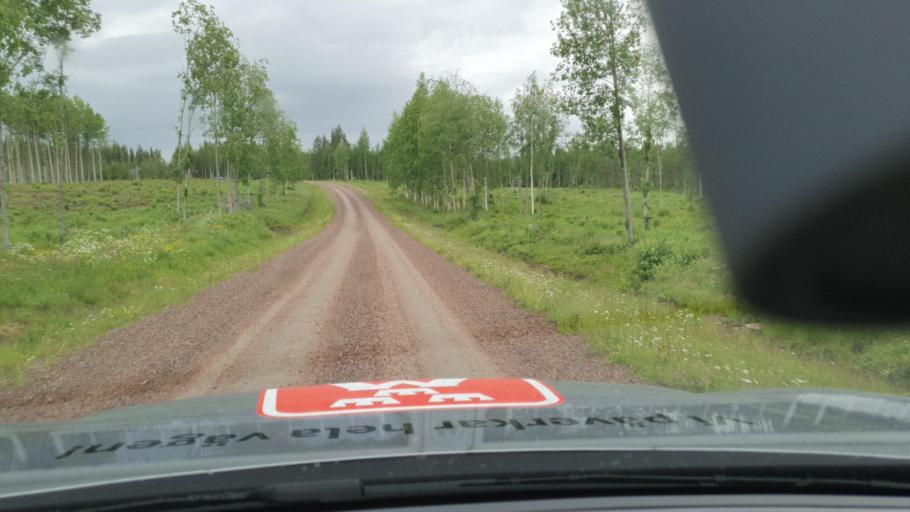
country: SE
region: Norrbotten
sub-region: Overkalix Kommun
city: OEverkalix
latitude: 66.6048
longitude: 22.7472
